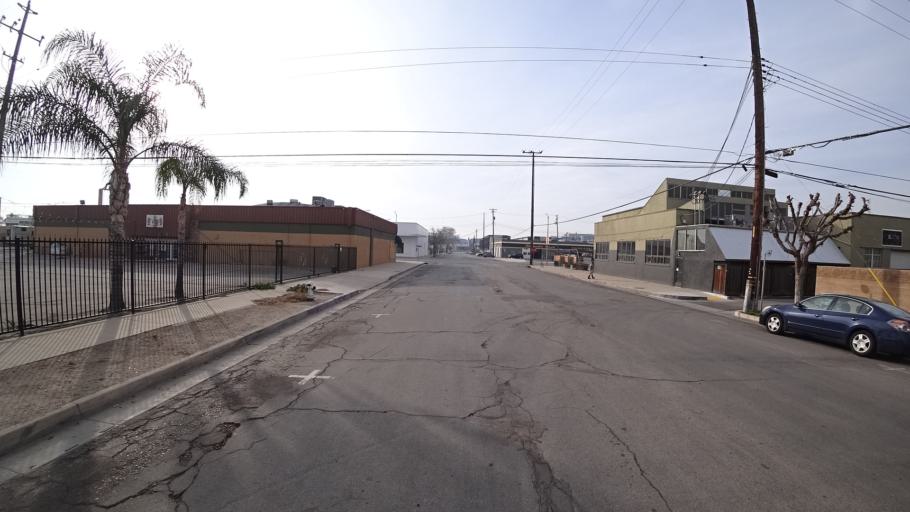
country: US
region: California
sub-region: Kern County
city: Bakersfield
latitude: 35.3768
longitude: -119.0129
